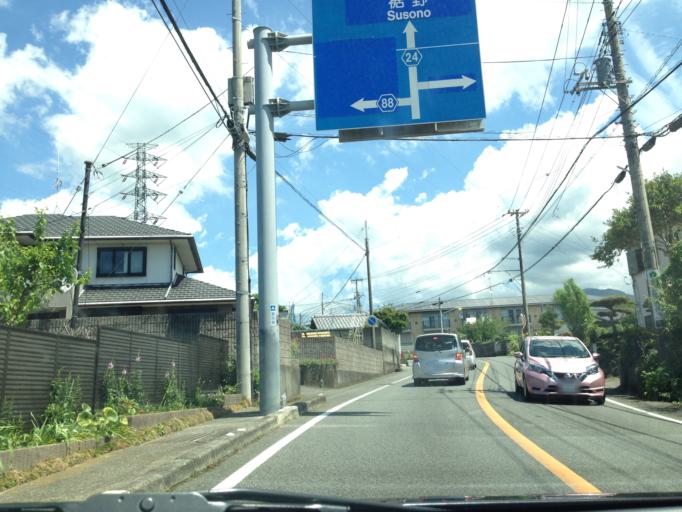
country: JP
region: Shizuoka
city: Fuji
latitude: 35.1861
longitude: 138.7035
